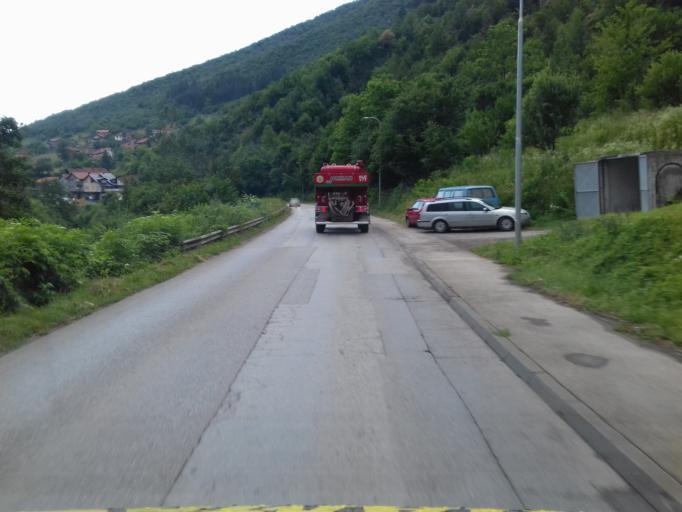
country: BA
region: Federation of Bosnia and Herzegovina
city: Visoko
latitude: 43.9706
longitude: 18.1861
